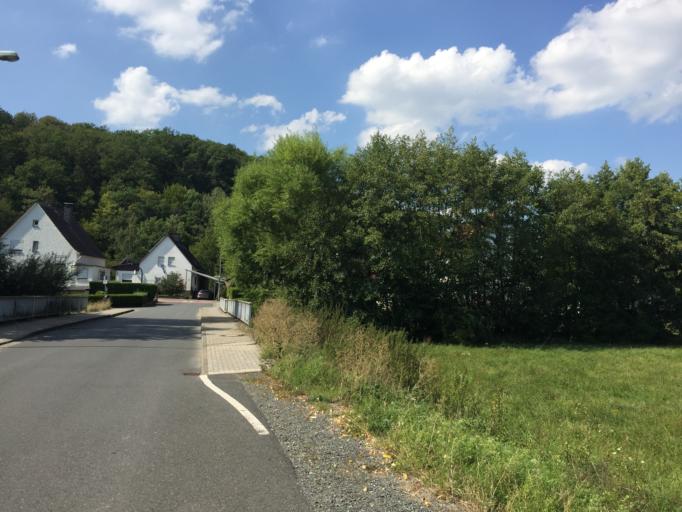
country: DE
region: Hesse
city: Solms
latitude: 50.5216
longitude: 8.4097
